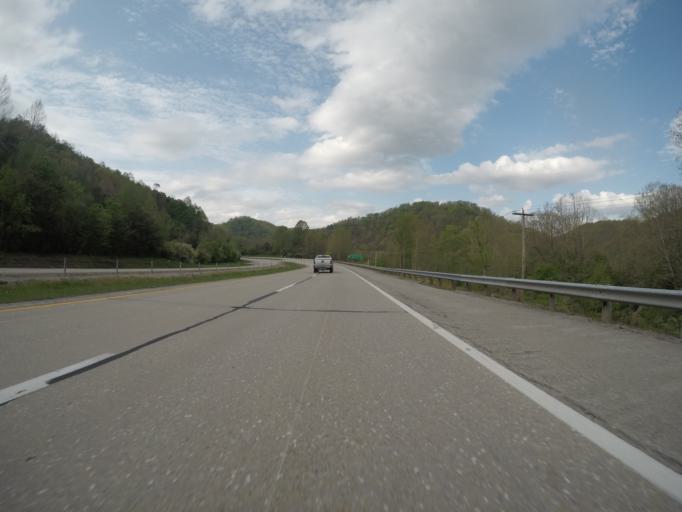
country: US
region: West Virginia
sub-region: Boone County
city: Madison
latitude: 38.1111
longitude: -81.8482
